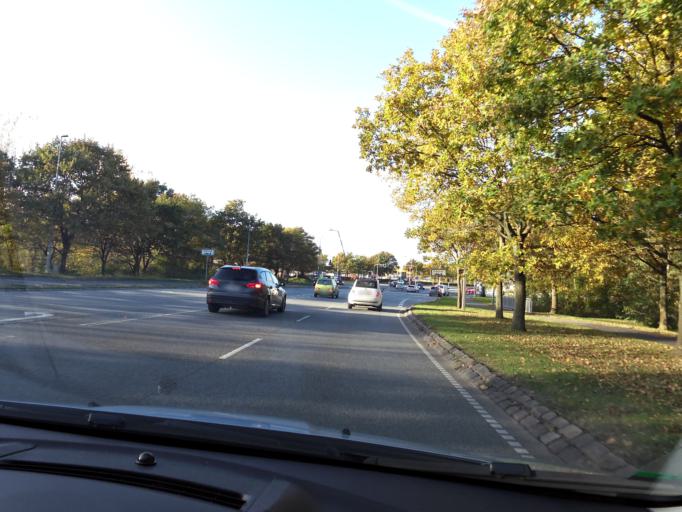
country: DK
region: South Denmark
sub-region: Odense Kommune
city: Neder Holluf
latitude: 55.3759
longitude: 10.4369
